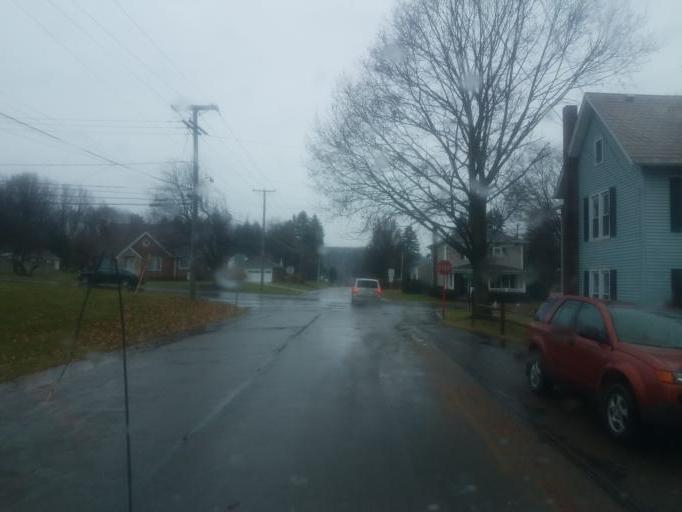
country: US
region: Ohio
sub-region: Sandusky County
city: Bellville
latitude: 40.6196
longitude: -82.5150
